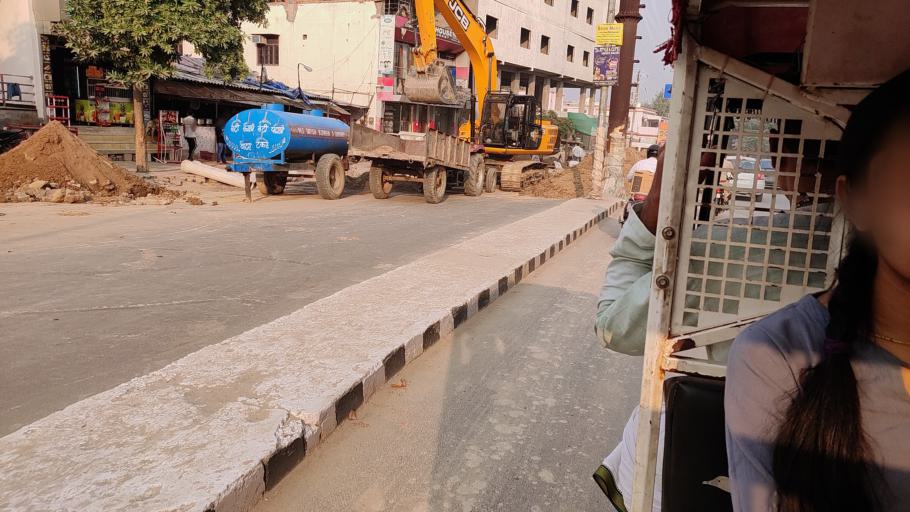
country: IN
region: Uttar Pradesh
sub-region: Mathura
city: Mathura
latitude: 27.5097
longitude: 77.6701
